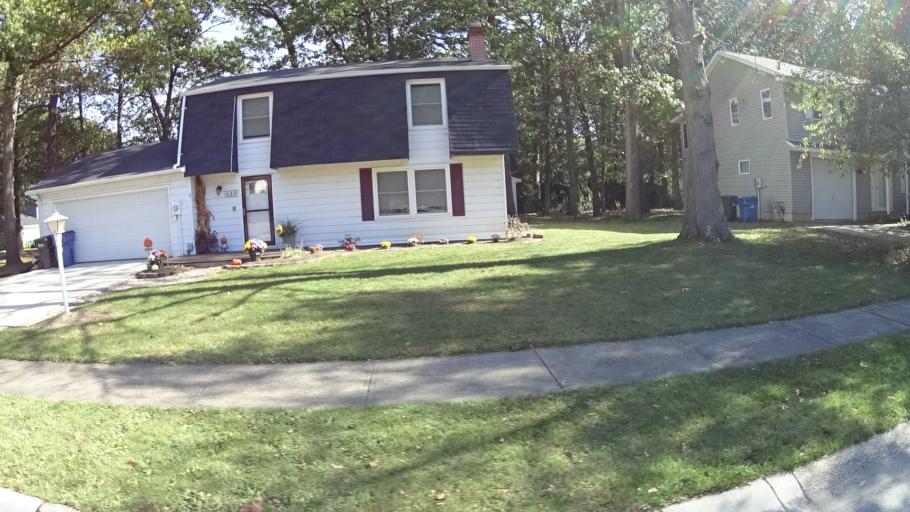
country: US
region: Ohio
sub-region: Lorain County
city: Vermilion-on-the-Lake
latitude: 41.4212
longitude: -82.3080
